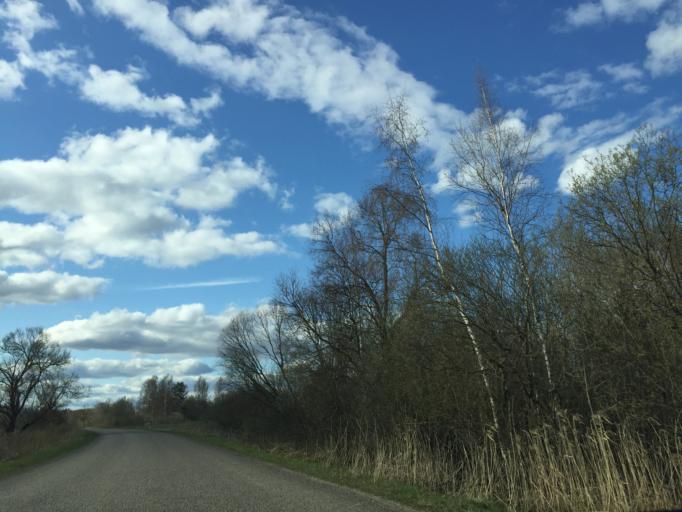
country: LV
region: Rezekne
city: Rezekne
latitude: 56.6215
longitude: 27.3145
